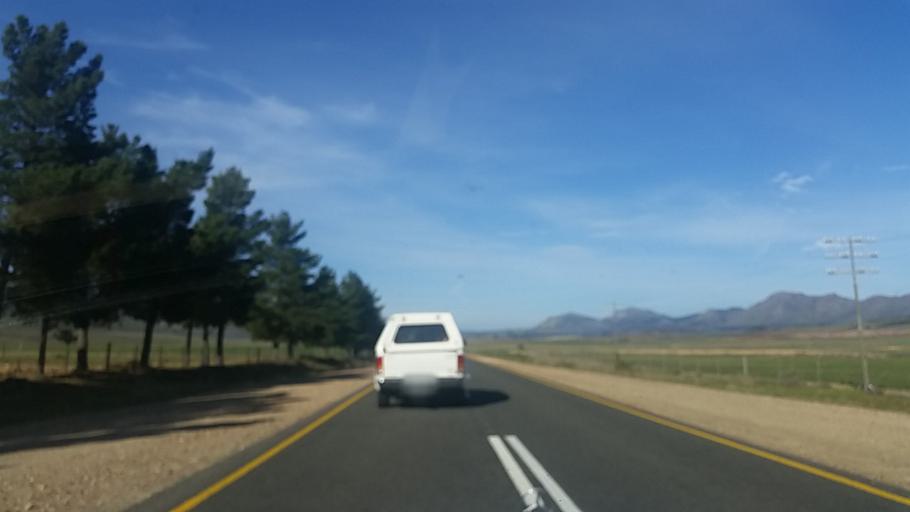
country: ZA
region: Western Cape
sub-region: Eden District Municipality
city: George
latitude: -33.8173
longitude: 22.5098
